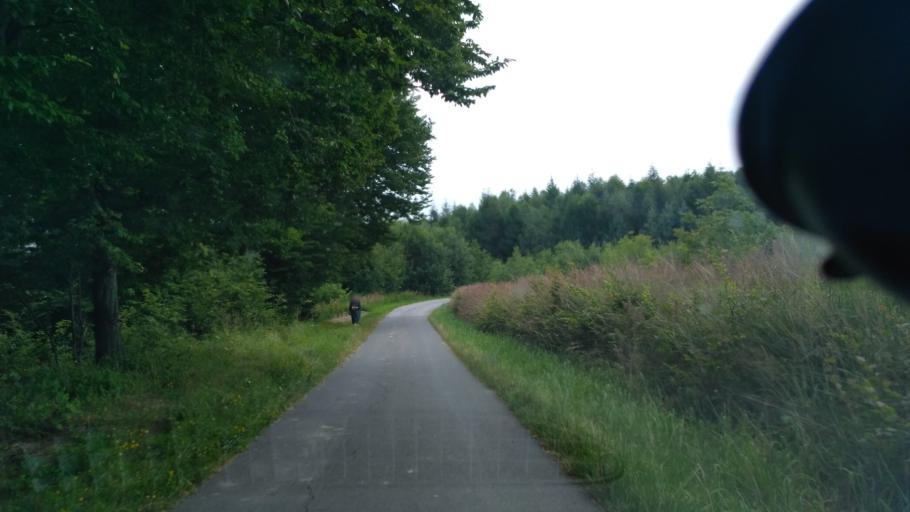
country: PL
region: Subcarpathian Voivodeship
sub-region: Powiat przeworski
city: Lopuszka Wielka
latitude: 49.9036
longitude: 22.4102
